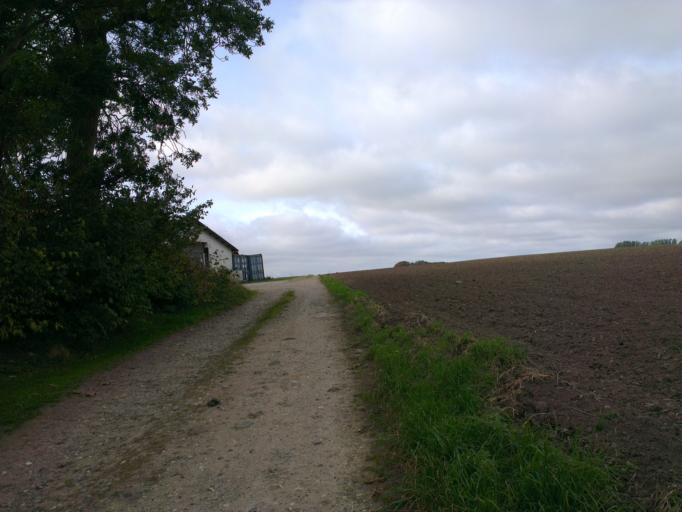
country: DK
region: Capital Region
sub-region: Frederikssund Kommune
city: Frederikssund
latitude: 55.8105
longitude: 12.0203
